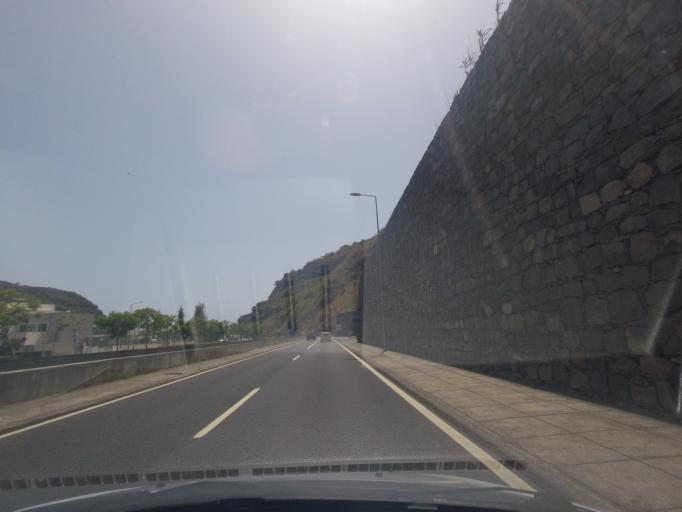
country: PT
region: Madeira
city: Ribeira Brava
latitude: 32.6776
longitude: -17.0623
